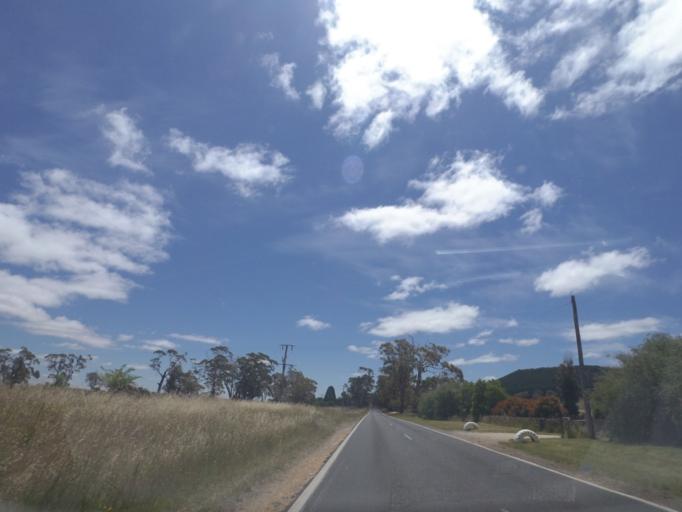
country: AU
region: Victoria
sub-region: Mount Alexander
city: Castlemaine
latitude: -37.2778
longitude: 144.1493
